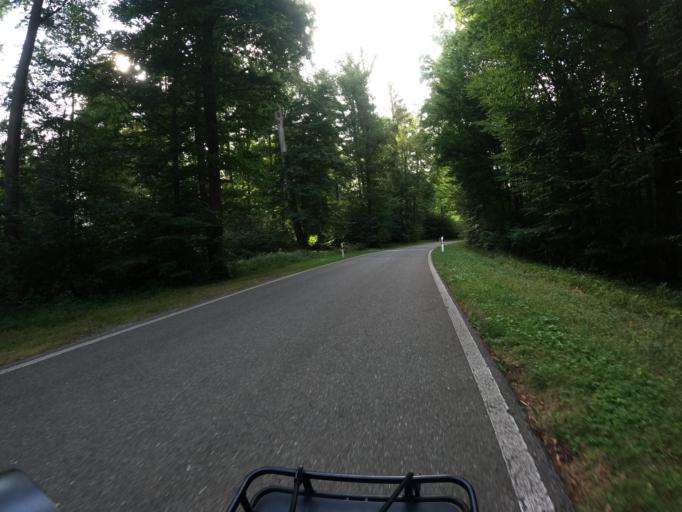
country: CH
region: Zurich
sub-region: Bezirk Dietikon
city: Urdorf / Oberurdorf
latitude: 47.3667
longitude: 8.4190
